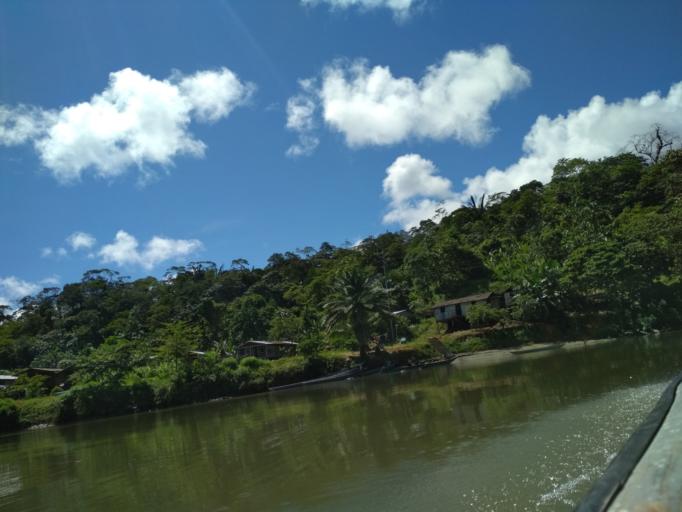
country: CO
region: Cauca
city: Timbiqui
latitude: 2.7594
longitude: -77.6628
